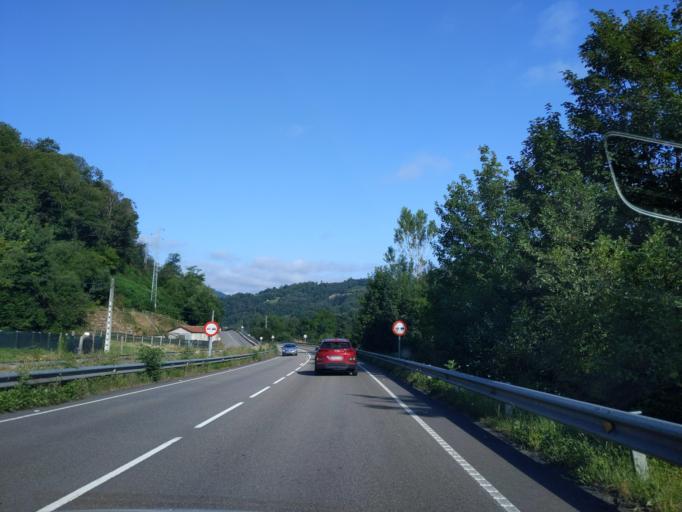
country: ES
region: Asturias
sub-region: Province of Asturias
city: Pola de Laviana
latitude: 43.2342
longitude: -5.5359
